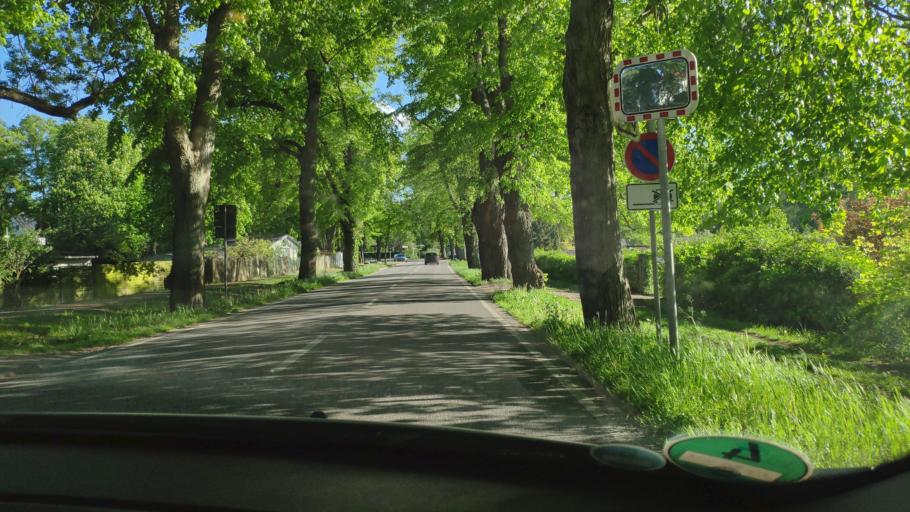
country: DE
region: Mecklenburg-Vorpommern
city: Neustrelitz
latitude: 53.3577
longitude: 13.0509
